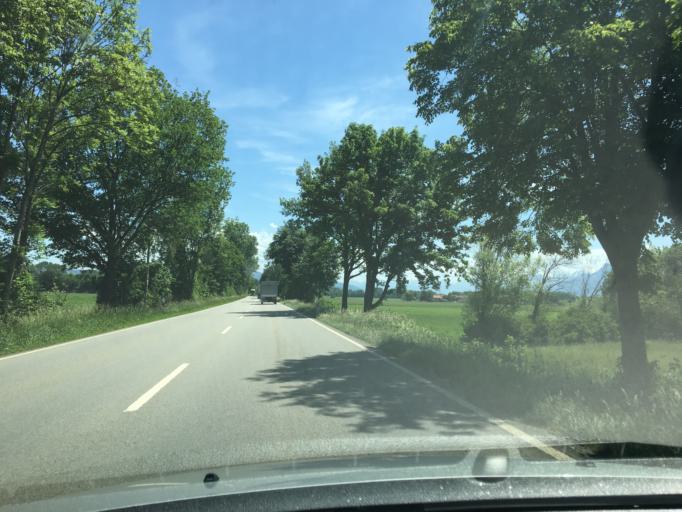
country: DE
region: Bavaria
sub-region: Upper Bavaria
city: Laufen
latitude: 47.8985
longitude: 12.9517
